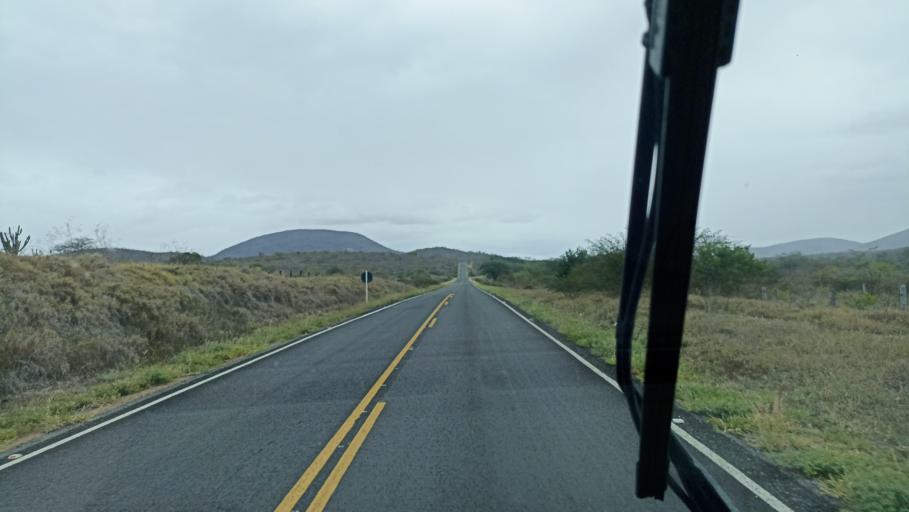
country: BR
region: Bahia
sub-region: Andarai
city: Vera Cruz
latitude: -13.0481
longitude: -40.7590
